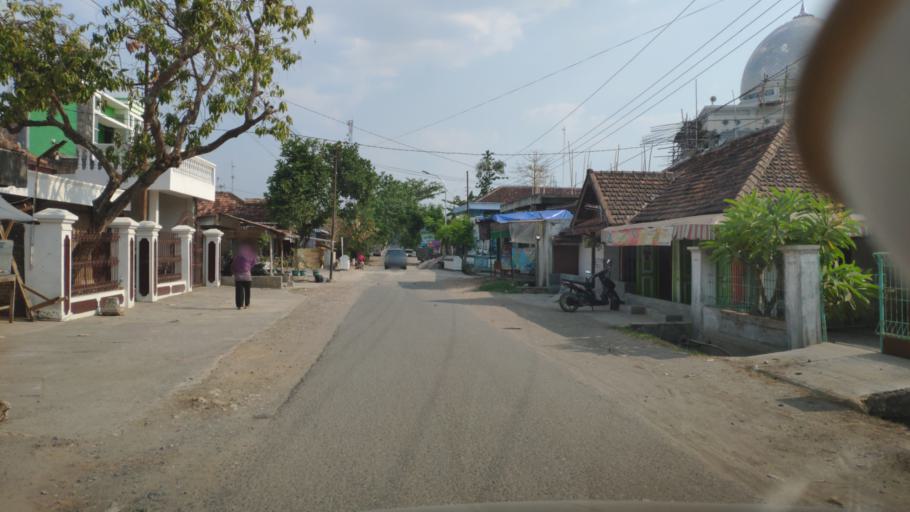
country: ID
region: Central Java
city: Jagong
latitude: -7.0512
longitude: 111.2391
